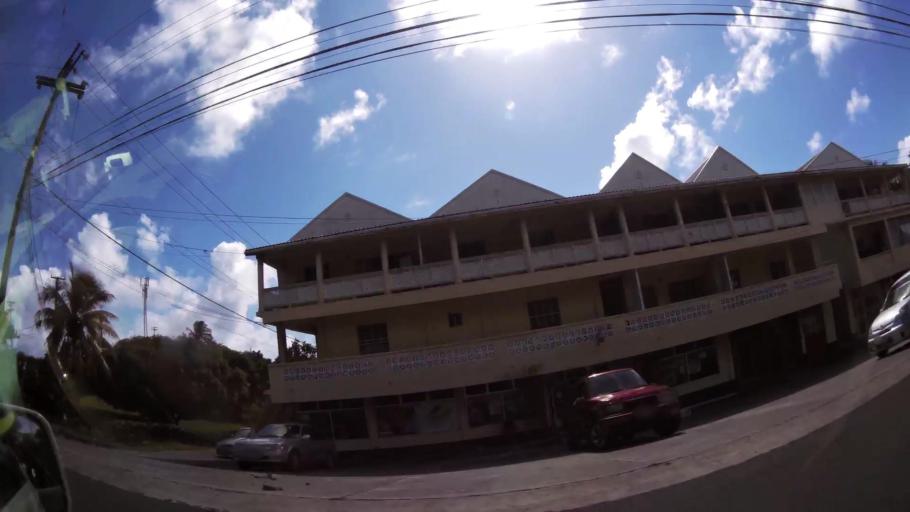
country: VC
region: Saint George
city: Kingstown
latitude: 13.1339
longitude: -61.1834
